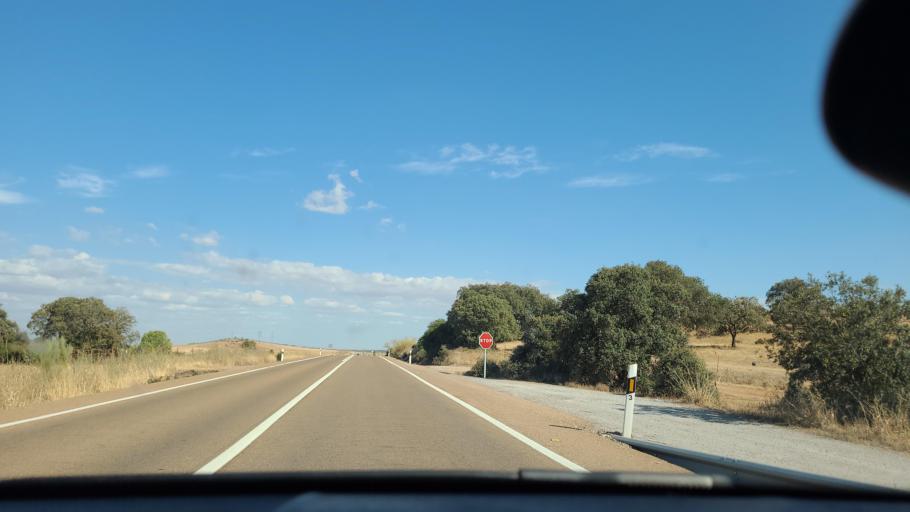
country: ES
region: Extremadura
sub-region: Provincia de Badajoz
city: Usagre
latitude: 38.3649
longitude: -6.2314
